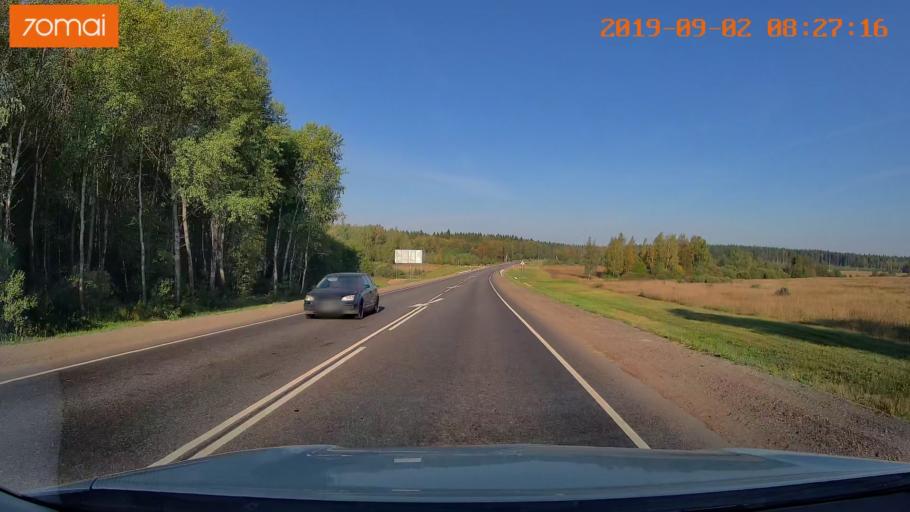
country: RU
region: Kaluga
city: Maloyaroslavets
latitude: 54.9807
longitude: 36.4206
